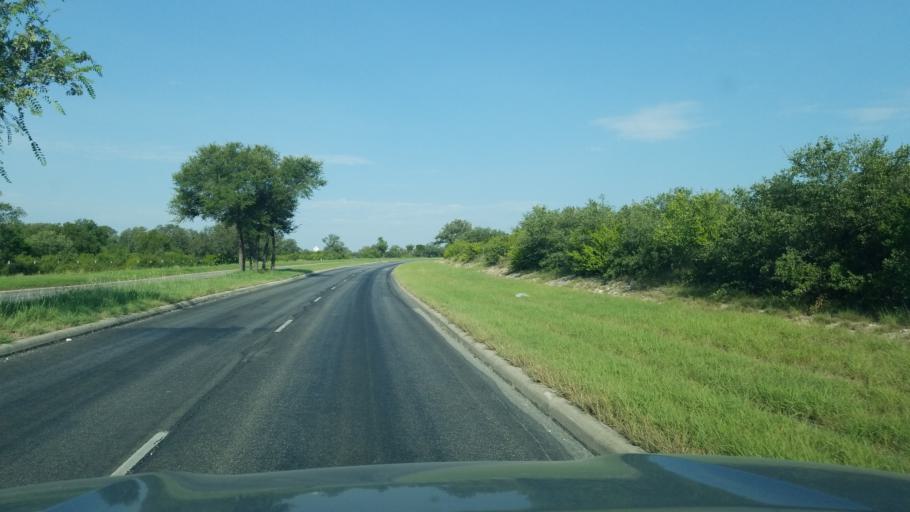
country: US
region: Texas
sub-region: Bexar County
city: Leon Valley
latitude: 29.4599
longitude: -98.7393
